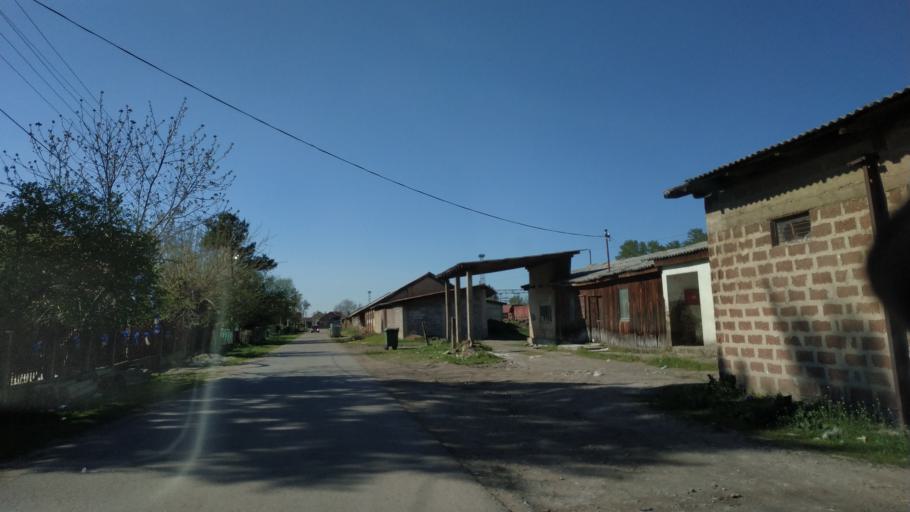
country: RS
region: Central Serbia
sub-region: Nisavski Okrug
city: Aleksinac
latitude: 43.5057
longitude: 21.6956
